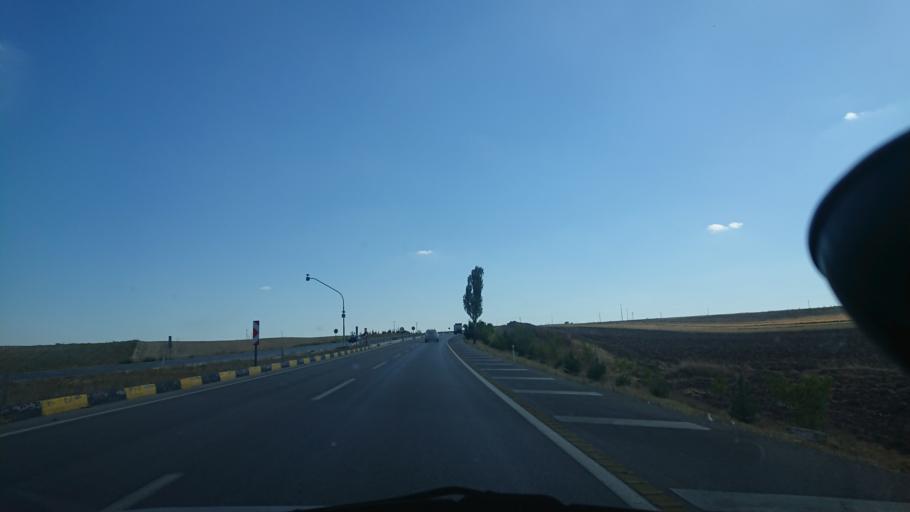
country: TR
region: Eskisehir
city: Mahmudiye
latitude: 39.5164
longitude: 30.9629
